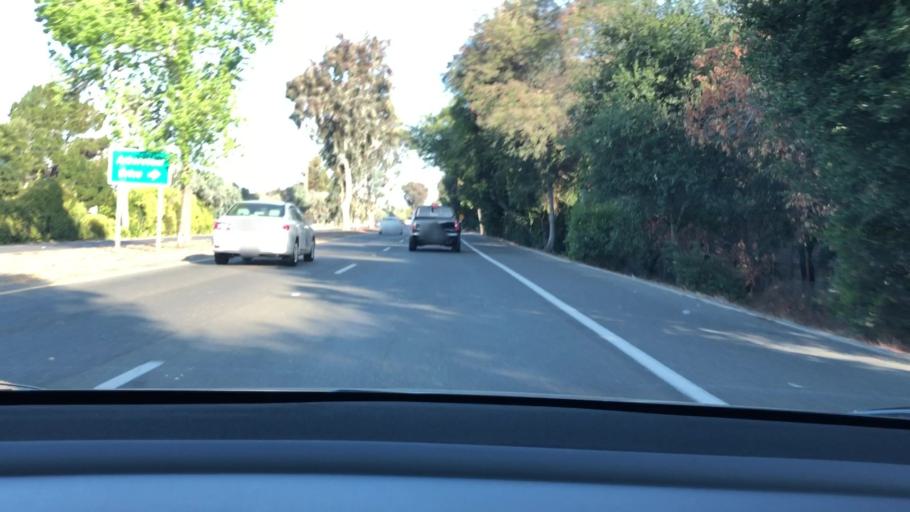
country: US
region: California
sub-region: Santa Clara County
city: Loyola
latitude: 37.3427
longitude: -122.0745
